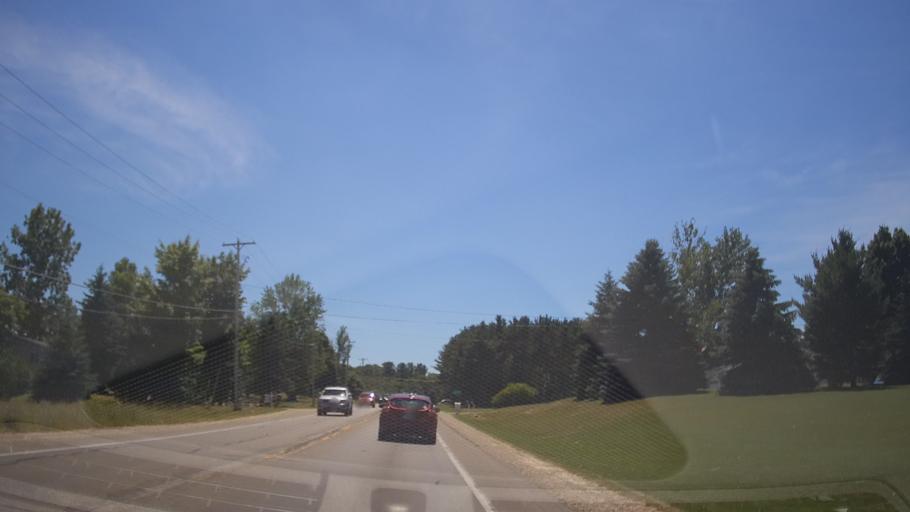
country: US
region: Michigan
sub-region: Grand Traverse County
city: Traverse City
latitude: 44.7185
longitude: -85.6845
